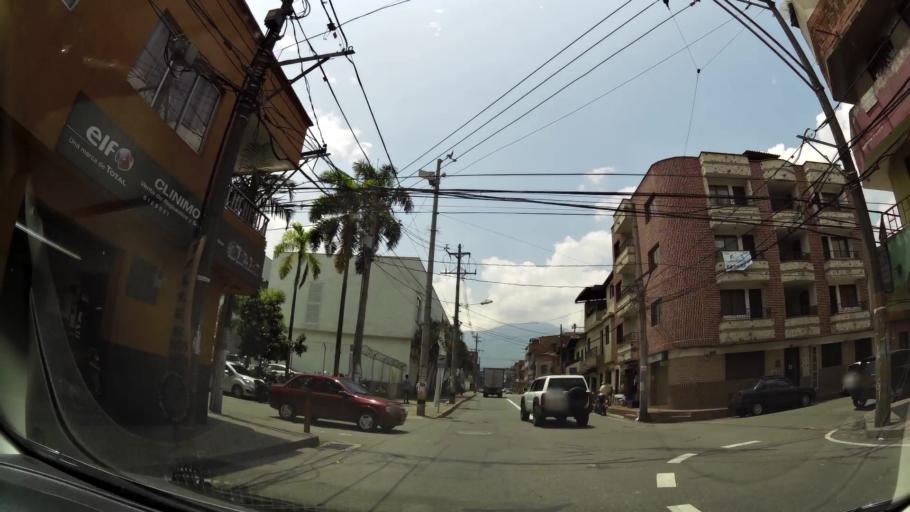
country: CO
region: Antioquia
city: Itagui
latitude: 6.1723
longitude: -75.6129
